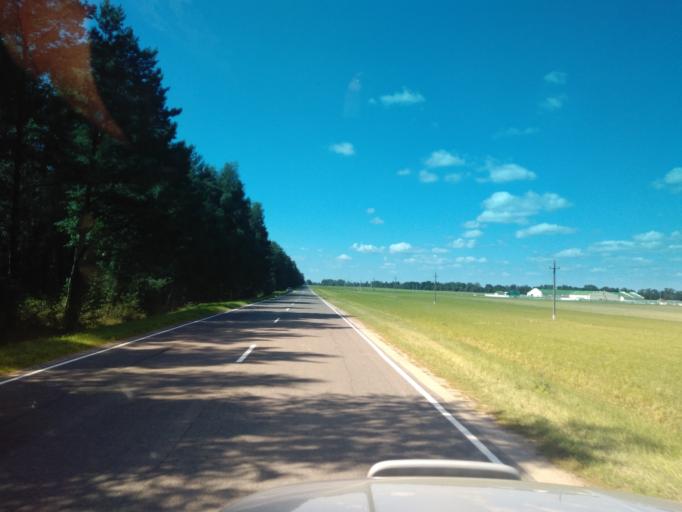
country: BY
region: Minsk
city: Stan'kava
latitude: 53.6241
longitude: 27.2836
